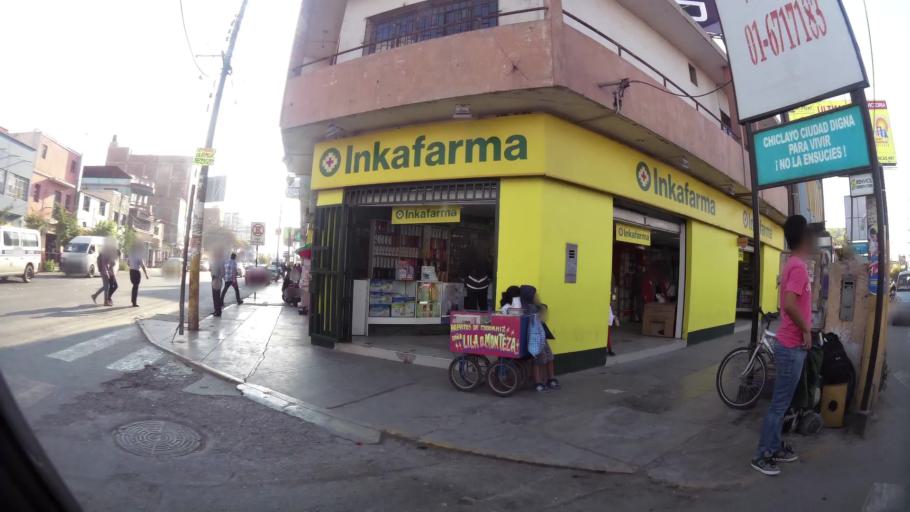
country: PE
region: Lambayeque
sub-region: Provincia de Chiclayo
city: Chiclayo
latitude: -6.7758
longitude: -79.8357
